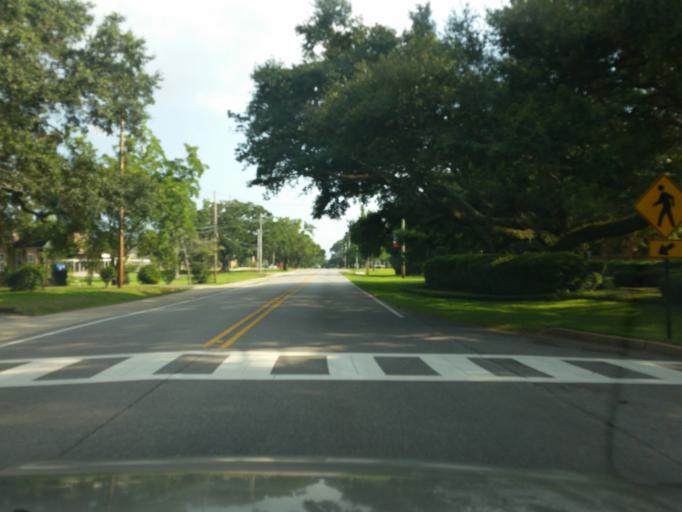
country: US
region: Alabama
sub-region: Baldwin County
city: Daphne
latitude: 30.5950
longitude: -87.9028
